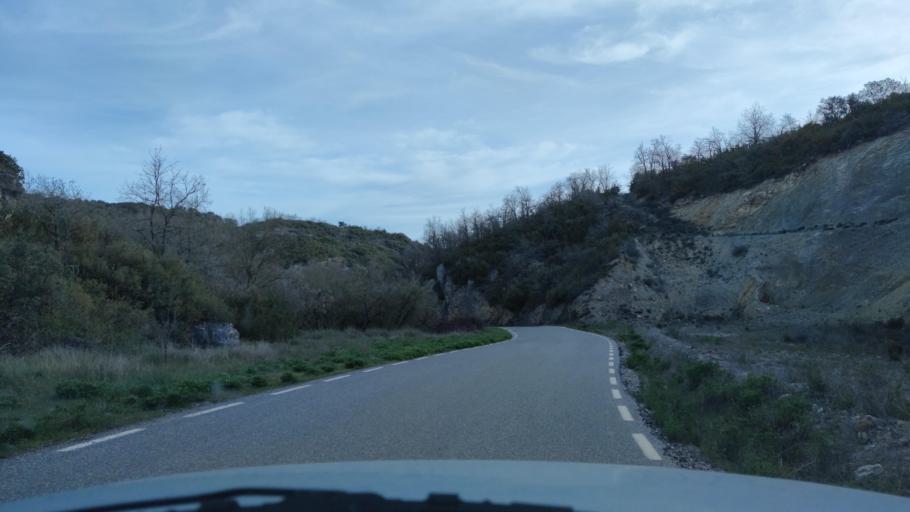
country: ES
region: Catalonia
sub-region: Provincia de Lleida
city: Os de Balaguer
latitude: 41.8852
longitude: 0.7905
